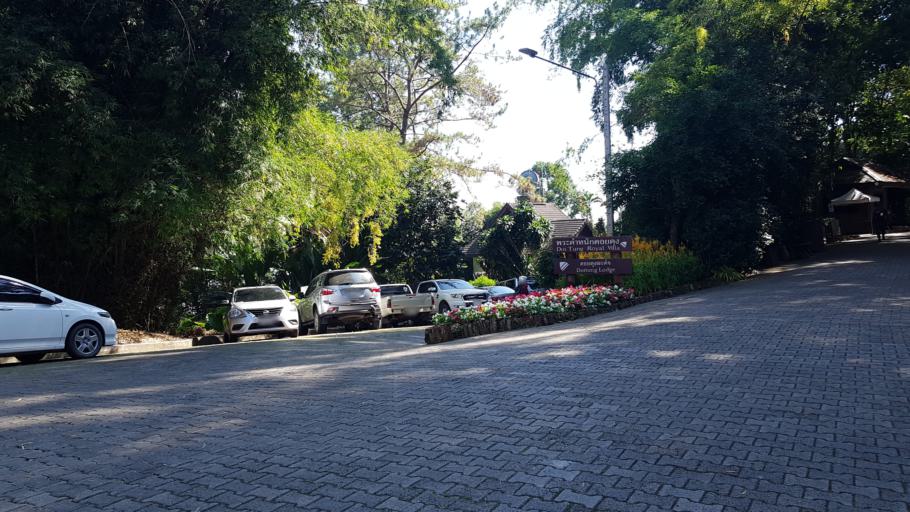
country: TH
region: Chiang Rai
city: Mae Fa Luang
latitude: 20.2887
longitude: 99.8112
